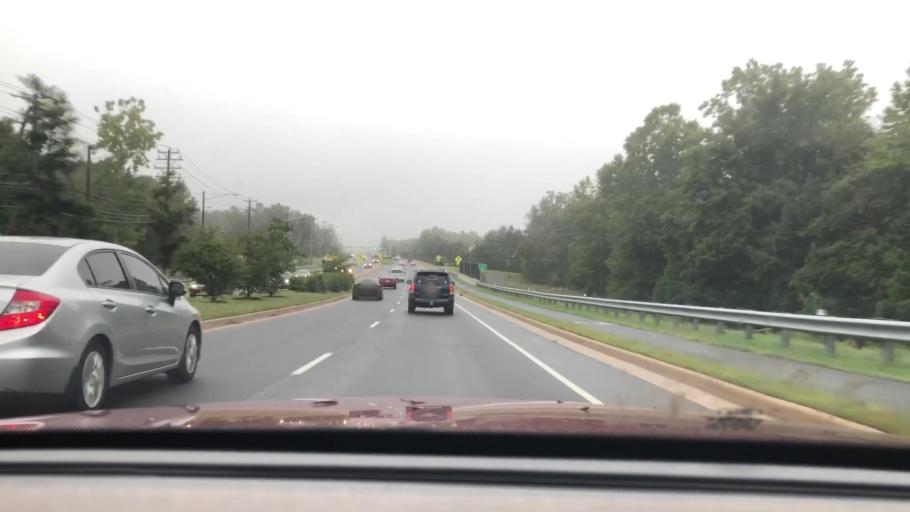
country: US
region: Virginia
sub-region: Fairfax County
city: Greenbriar
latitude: 38.8692
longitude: -77.4078
